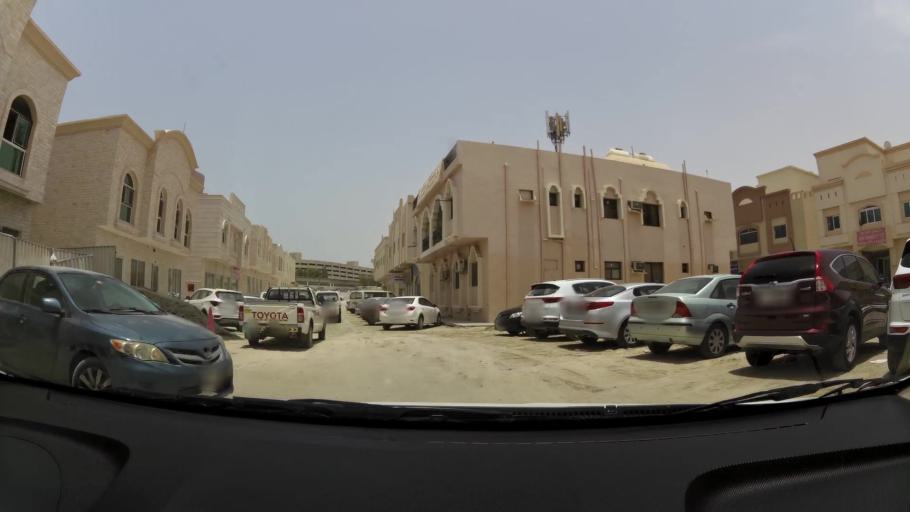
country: AE
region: Ash Shariqah
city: Sharjah
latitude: 25.3518
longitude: 55.4000
